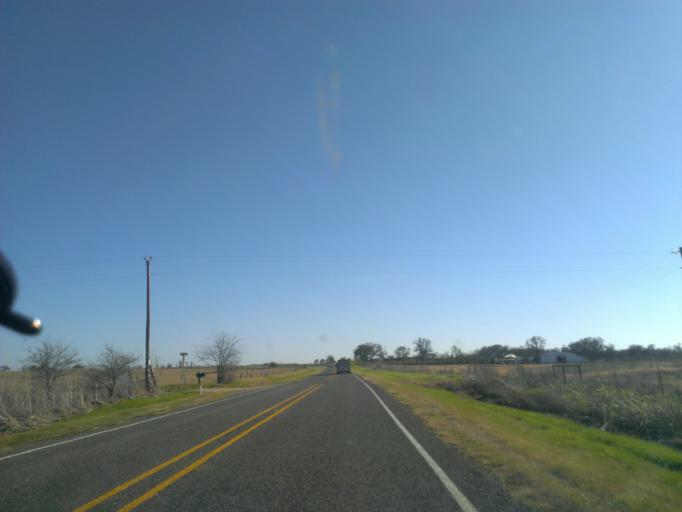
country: US
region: Texas
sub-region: Milam County
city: Thorndale
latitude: 30.5277
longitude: -97.2512
